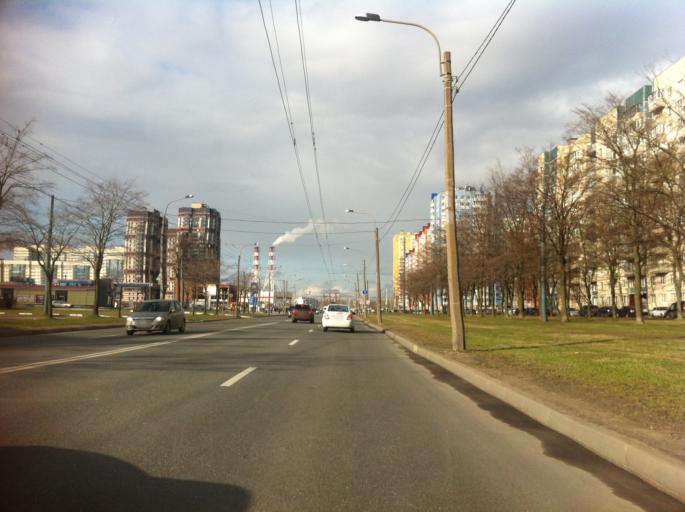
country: RU
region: St.-Petersburg
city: Uritsk
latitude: 59.8595
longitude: 30.1781
